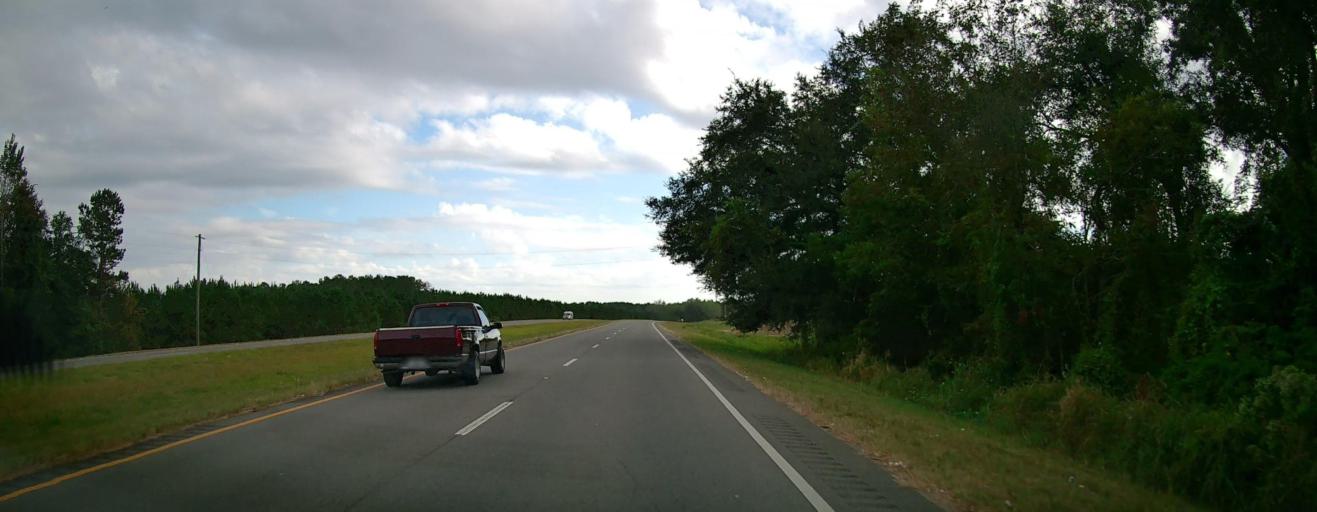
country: US
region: Georgia
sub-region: Thomas County
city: Meigs
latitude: 31.0632
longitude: -84.0737
